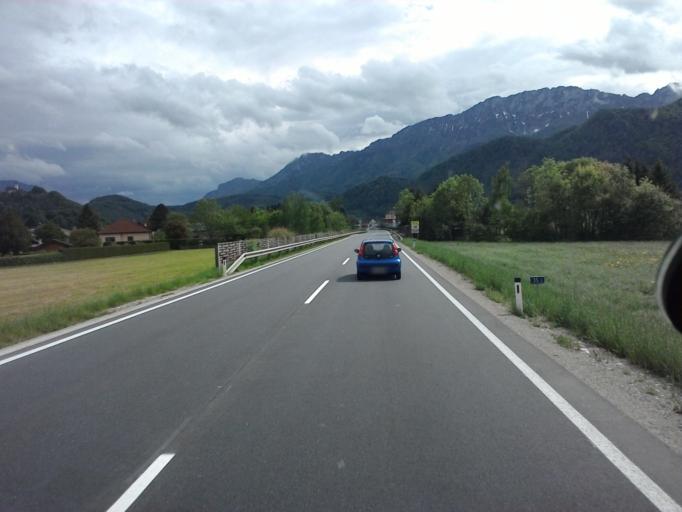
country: AT
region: Upper Austria
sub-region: Politischer Bezirk Kirchdorf an der Krems
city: Micheldorf in Oberoesterreich
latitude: 47.8875
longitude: 14.1282
